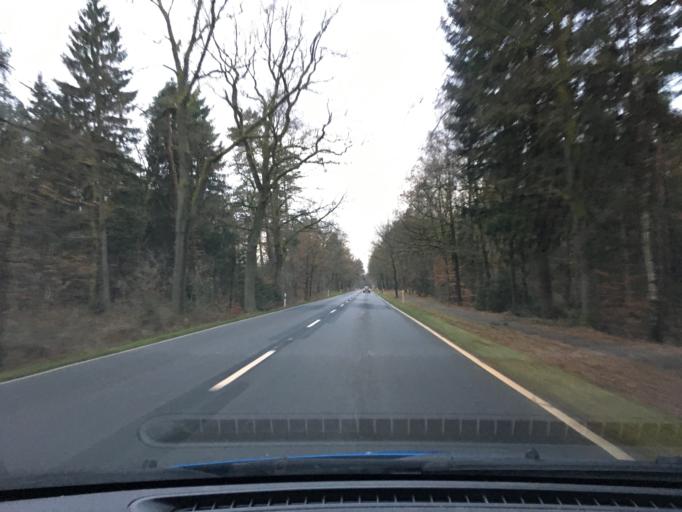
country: DE
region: Lower Saxony
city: Fassberg
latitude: 52.9650
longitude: 10.1942
